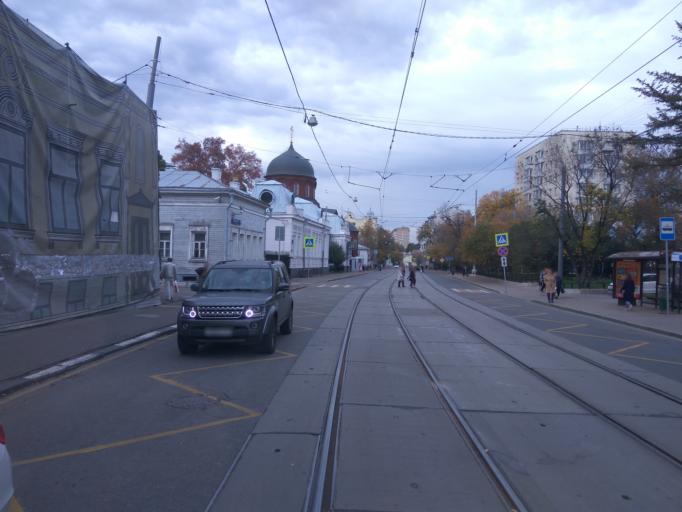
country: RU
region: Moscow
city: Zamoskvorech'ye
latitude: 55.7316
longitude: 37.6353
